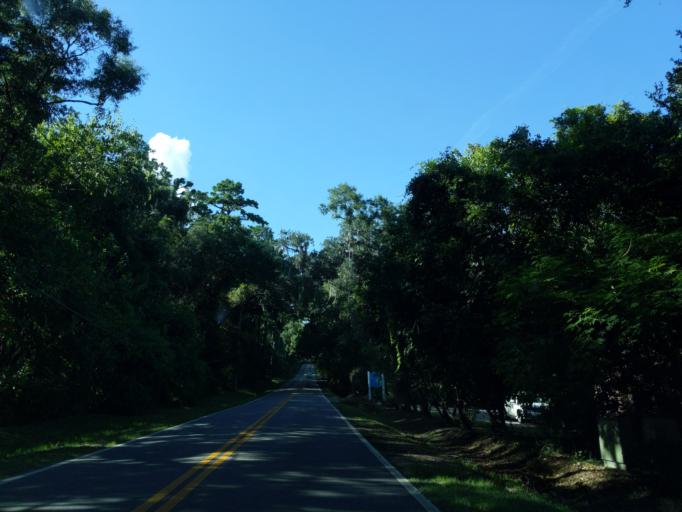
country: US
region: Florida
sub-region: Leon County
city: Tallahassee
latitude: 30.4213
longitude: -84.2436
